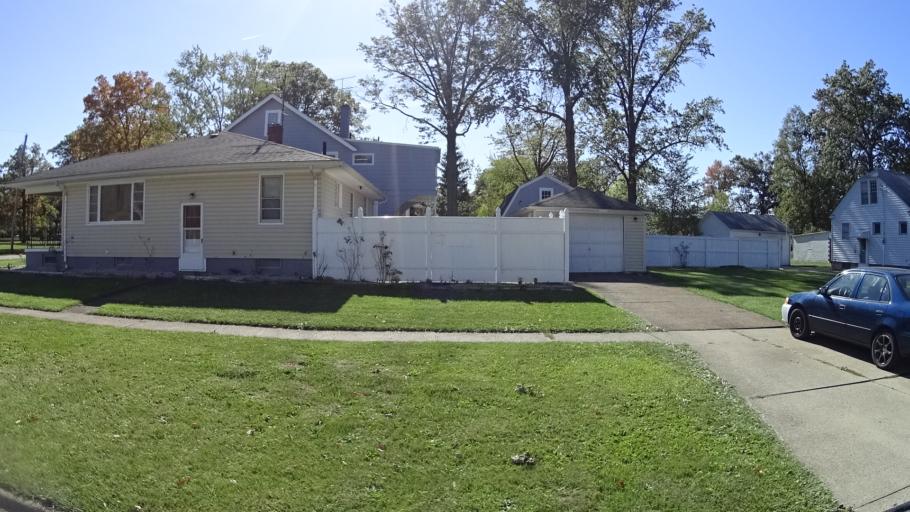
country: US
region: Ohio
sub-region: Lorain County
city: Lorain
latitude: 41.4448
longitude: -82.1756
